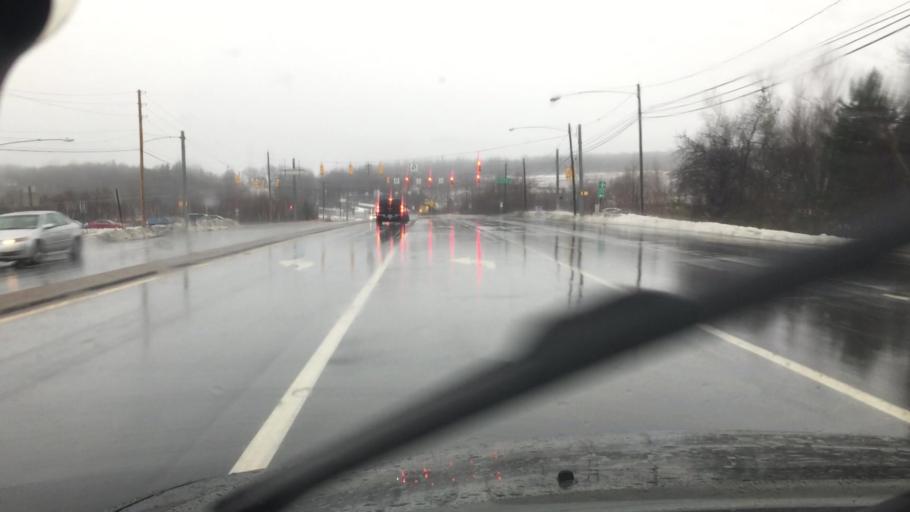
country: US
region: Pennsylvania
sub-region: Luzerne County
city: Harleigh
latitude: 40.9911
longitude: -75.9831
